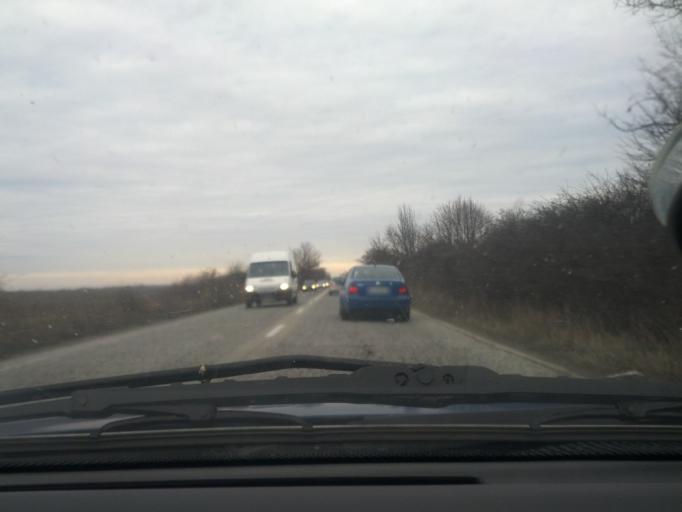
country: BG
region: Vratsa
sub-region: Obshtina Borovan
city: Borovan
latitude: 43.3793
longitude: 23.7133
